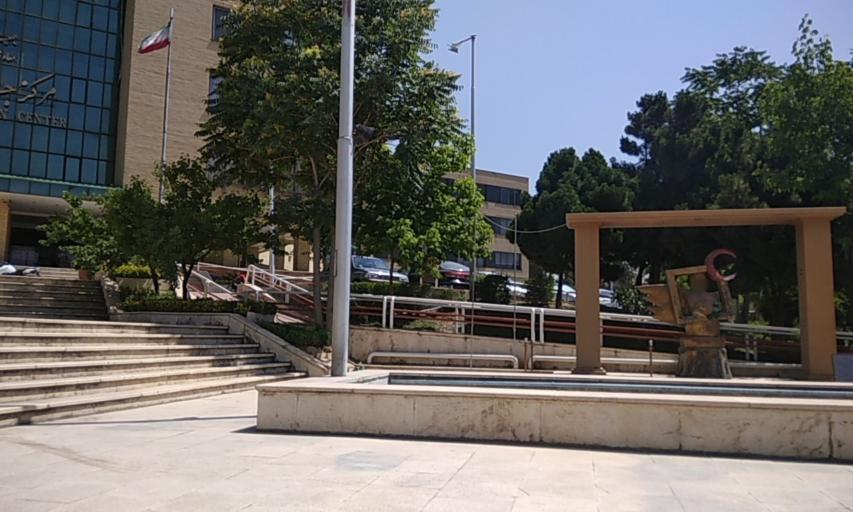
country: IR
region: Tehran
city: Tajrish
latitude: 35.7689
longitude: 51.4090
